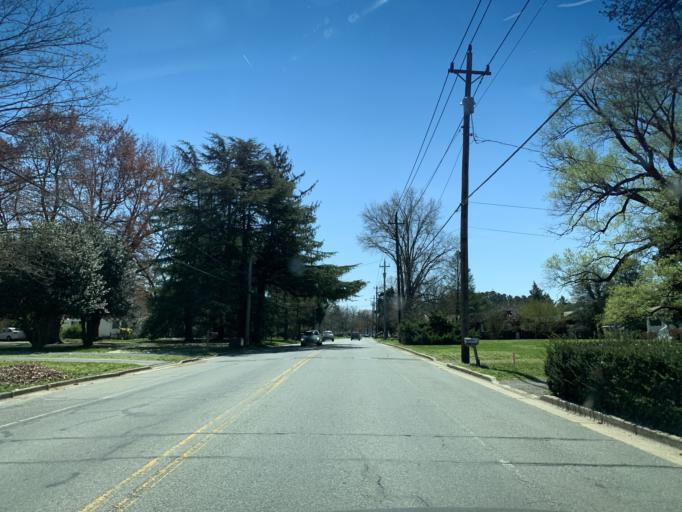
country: US
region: Maryland
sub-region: Talbot County
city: Easton
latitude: 38.7892
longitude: -76.0673
